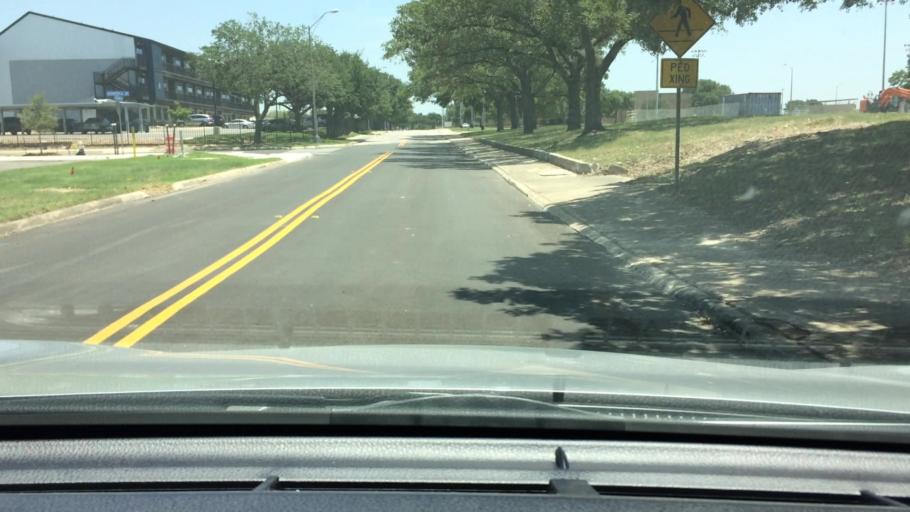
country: US
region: Texas
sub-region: Bexar County
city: San Antonio
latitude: 29.3416
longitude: -98.4495
